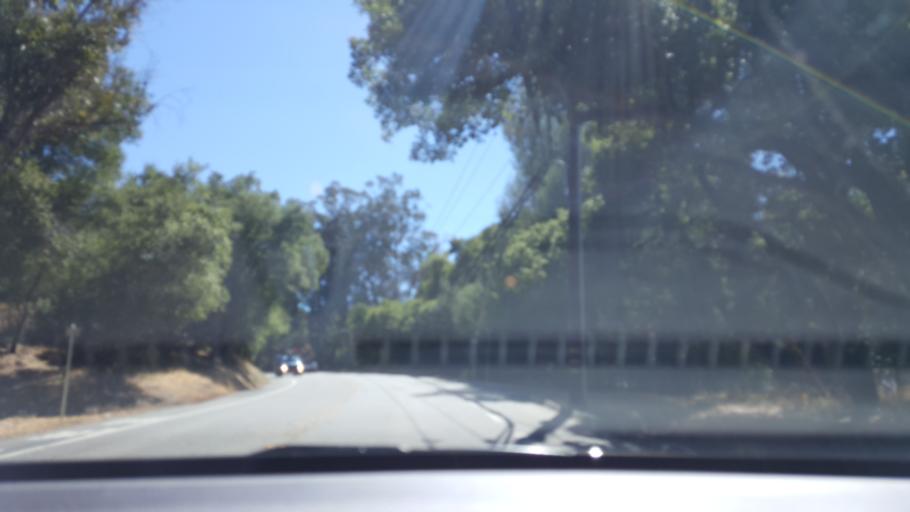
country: US
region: California
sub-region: San Mateo County
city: Woodside
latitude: 37.4089
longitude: -122.2443
